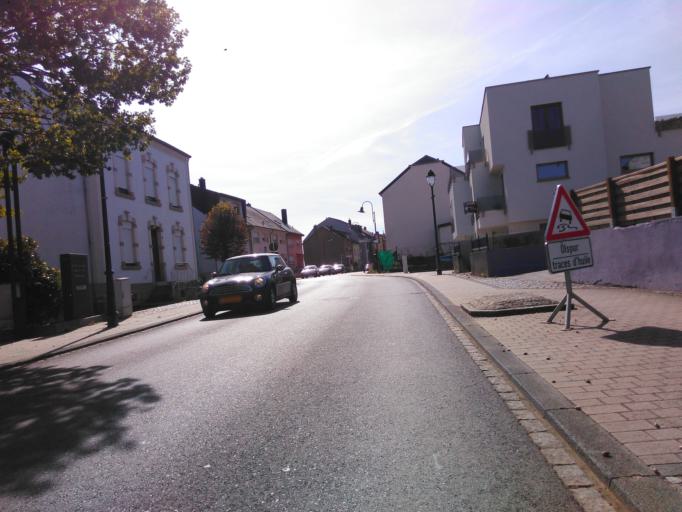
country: LU
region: Luxembourg
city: Tetange
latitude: 49.4769
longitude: 6.0356
